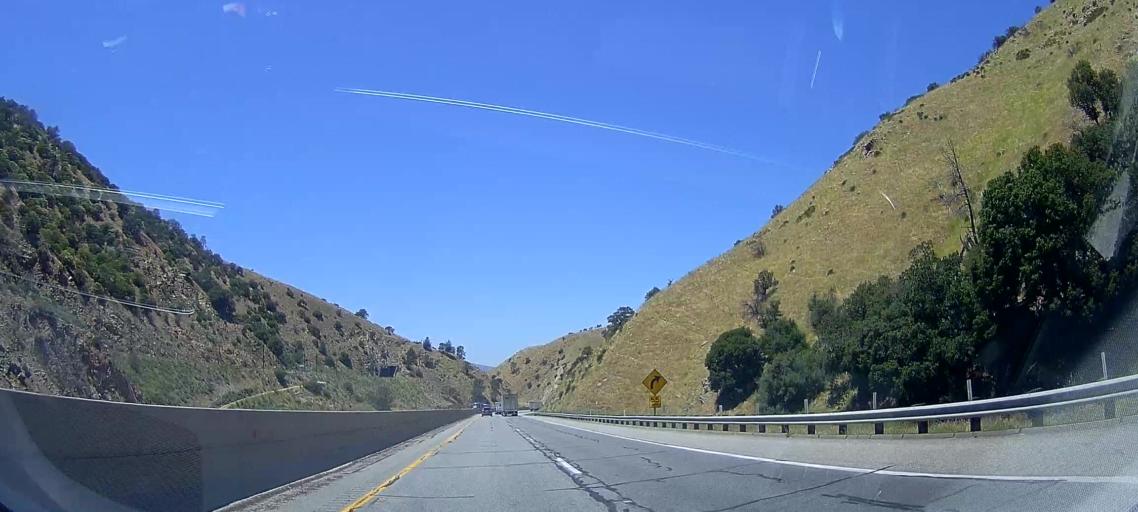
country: US
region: California
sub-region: Kern County
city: Golden Hills
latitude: 35.1787
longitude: -118.4843
